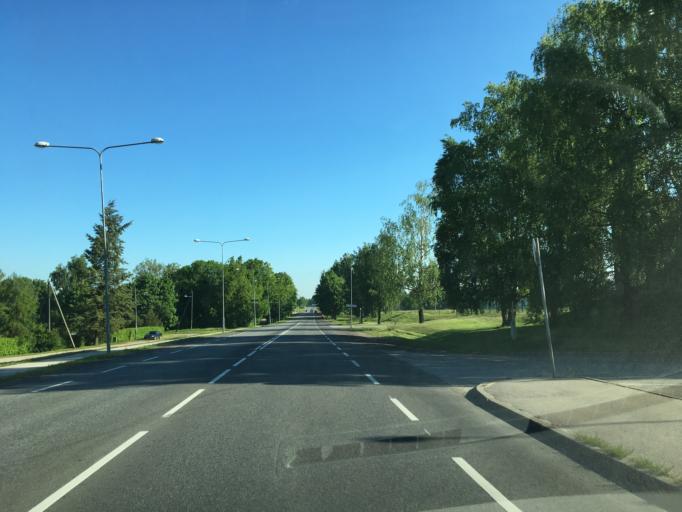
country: EE
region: Tartu
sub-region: Tartu linn
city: Tartu
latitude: 58.4002
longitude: 26.7084
